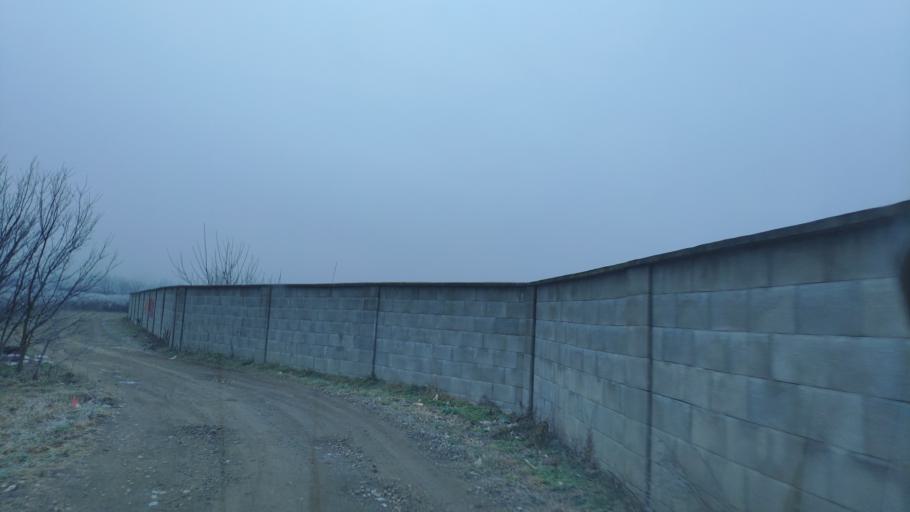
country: SK
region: Kosicky
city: Kosice
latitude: 48.6169
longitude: 21.3270
